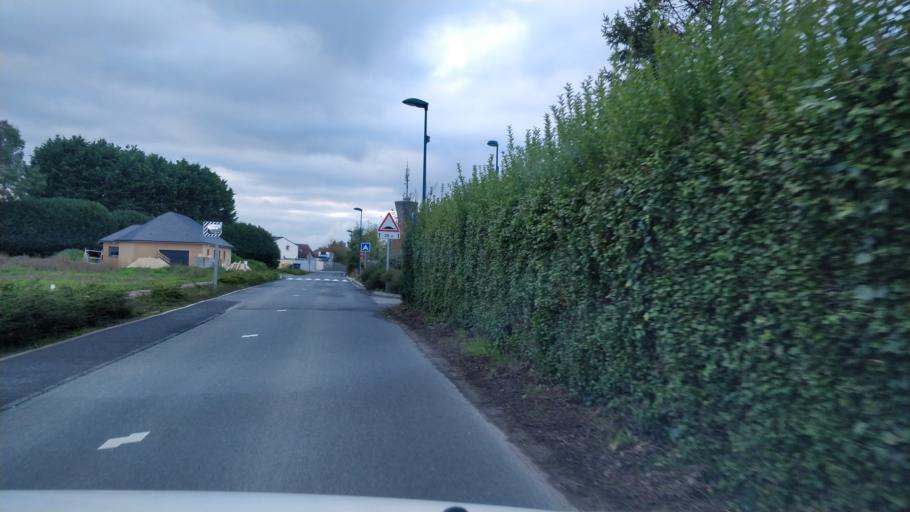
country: FR
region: Lower Normandy
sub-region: Departement du Calvados
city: Benouville
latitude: 49.2626
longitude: -0.2822
